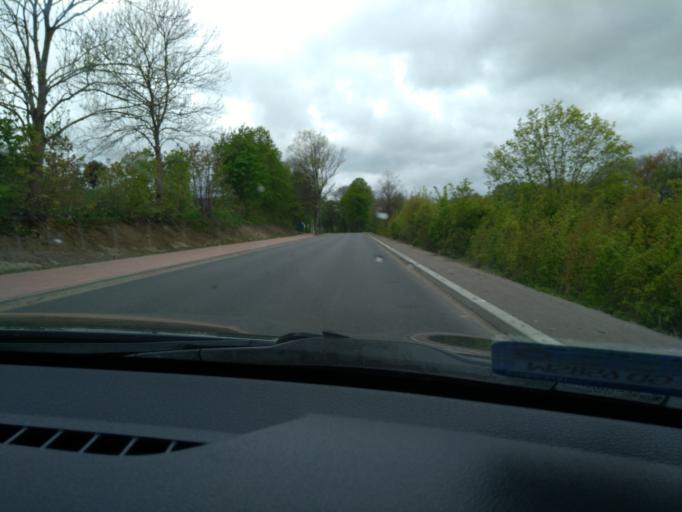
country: PL
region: Pomeranian Voivodeship
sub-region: Powiat kartuski
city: Garcz
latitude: 54.3472
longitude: 18.1231
